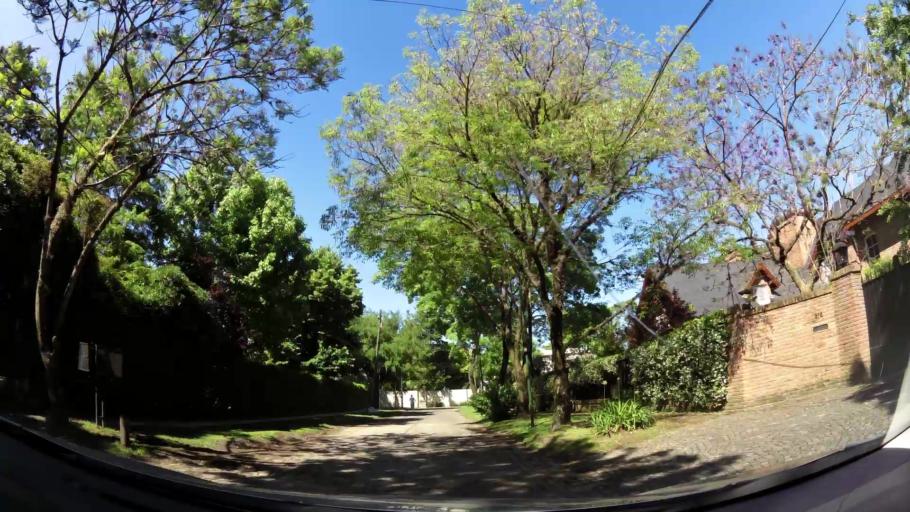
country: AR
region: Buenos Aires
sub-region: Partido de Tigre
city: Tigre
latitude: -34.4860
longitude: -58.5675
